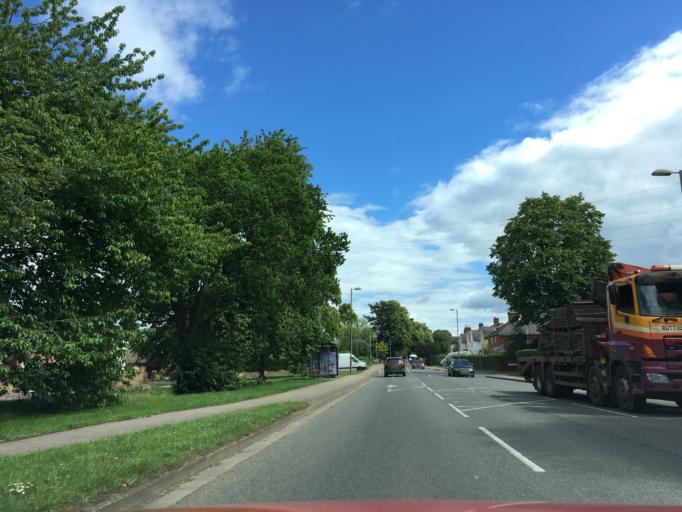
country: GB
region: England
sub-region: Oxfordshire
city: Banbury
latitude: 52.0534
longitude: -1.3455
